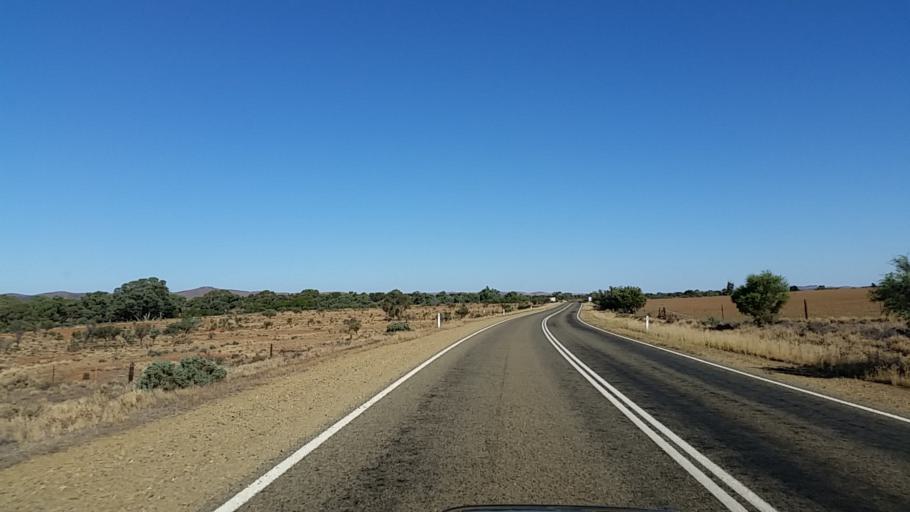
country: AU
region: South Australia
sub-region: Flinders Ranges
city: Quorn
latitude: -32.4149
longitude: 138.5223
